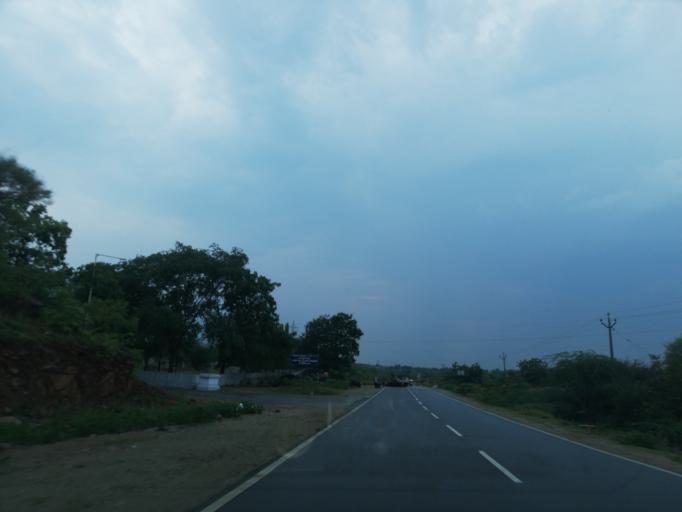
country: IN
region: Andhra Pradesh
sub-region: Guntur
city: Macherla
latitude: 16.6653
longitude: 79.2846
